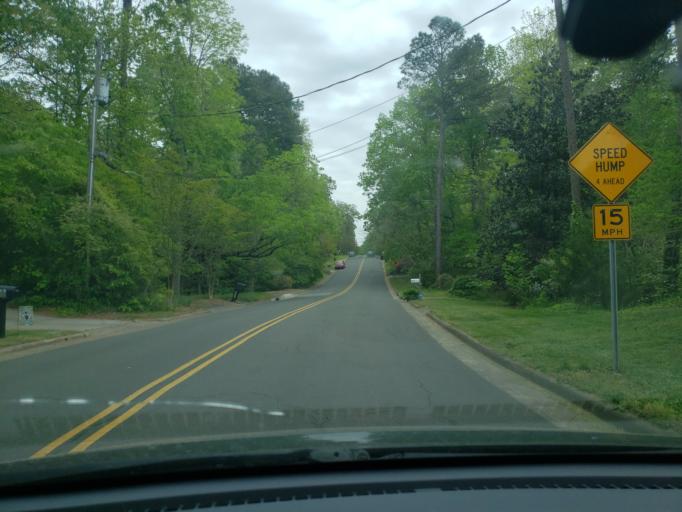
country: US
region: North Carolina
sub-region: Durham County
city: Durham
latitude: 35.9346
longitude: -78.9608
